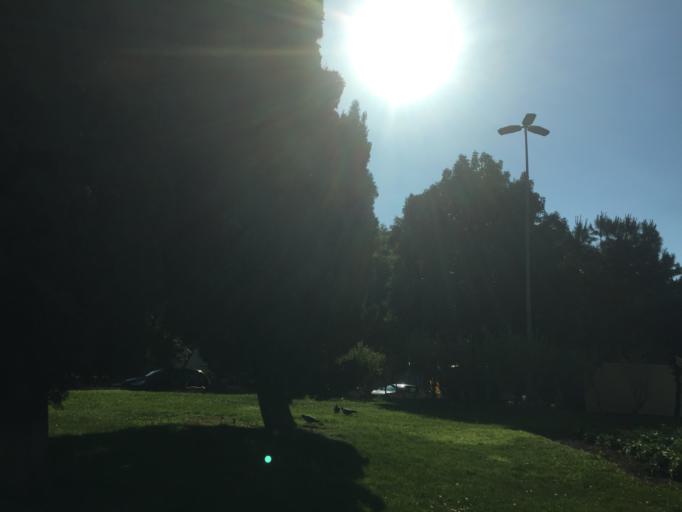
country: ES
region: Catalonia
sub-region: Provincia de Barcelona
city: Sant Marti
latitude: 41.4193
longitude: 2.1913
